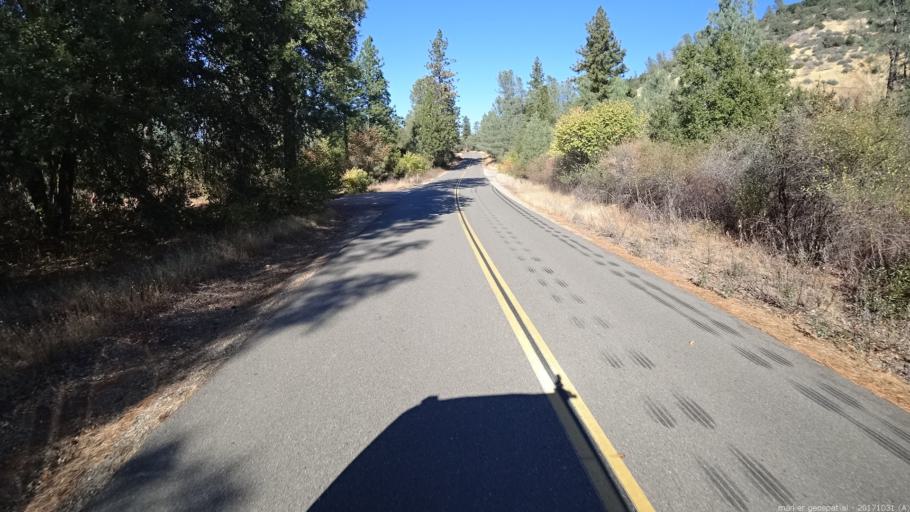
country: US
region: California
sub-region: Shasta County
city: Shingletown
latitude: 40.4524
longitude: -122.0067
